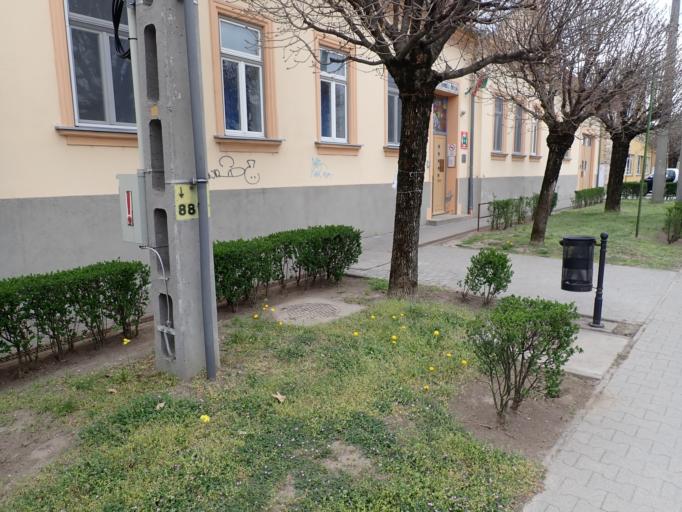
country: HU
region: Tolna
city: Paks
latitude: 46.6166
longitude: 18.8520
